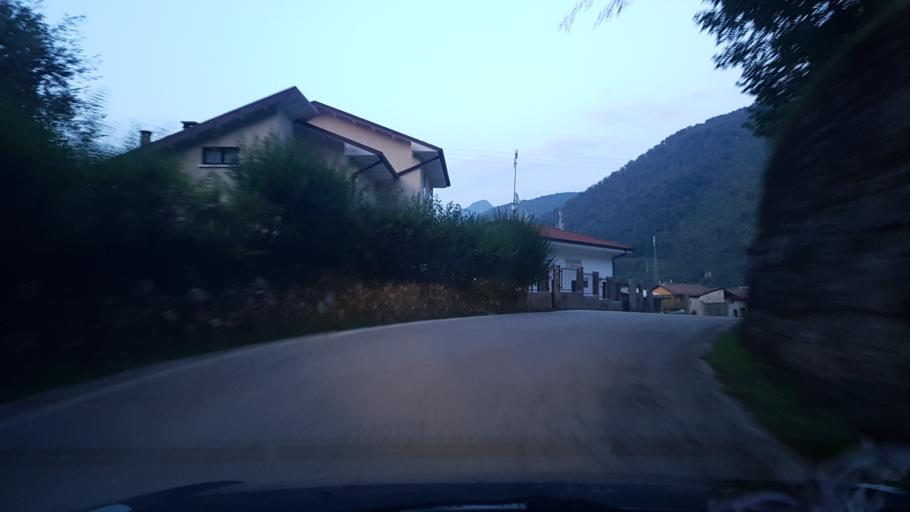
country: IT
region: Friuli Venezia Giulia
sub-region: Provincia di Pordenone
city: Frisanco
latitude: 46.2508
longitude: 12.7420
